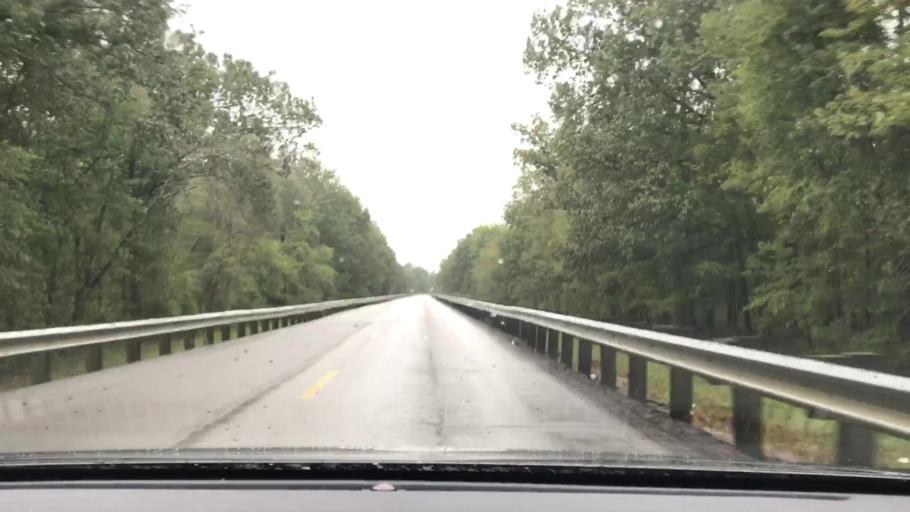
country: US
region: Kentucky
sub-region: McLean County
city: Calhoun
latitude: 37.3957
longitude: -87.2934
